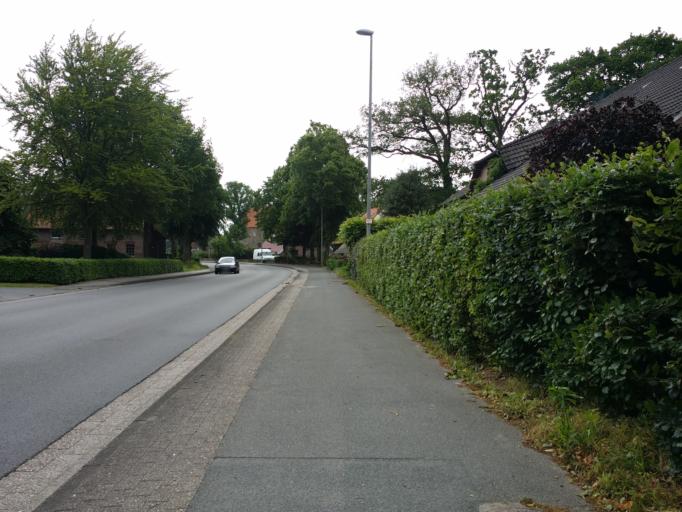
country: DE
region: Lower Saxony
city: Friedeburg
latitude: 53.4372
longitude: 7.8547
